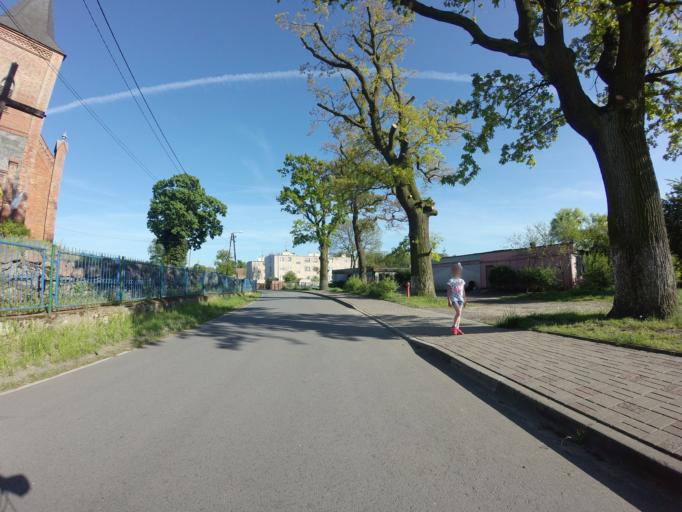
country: PL
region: West Pomeranian Voivodeship
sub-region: Powiat choszczenski
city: Pelczyce
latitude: 53.1181
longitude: 15.3227
